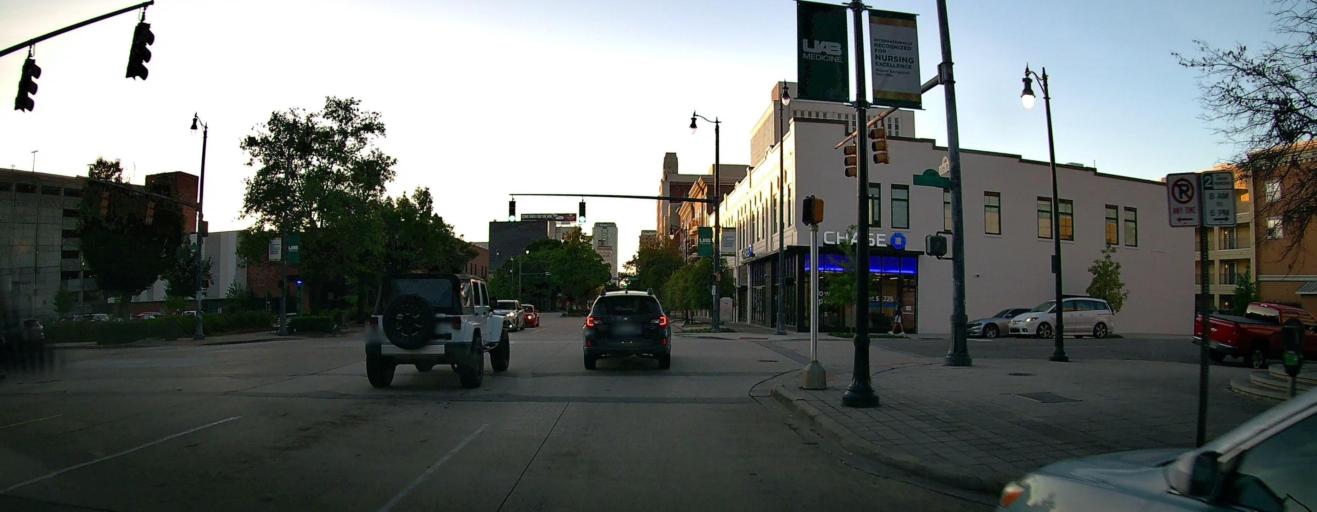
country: US
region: Alabama
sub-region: Jefferson County
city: Birmingham
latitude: 33.5078
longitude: -86.8012
